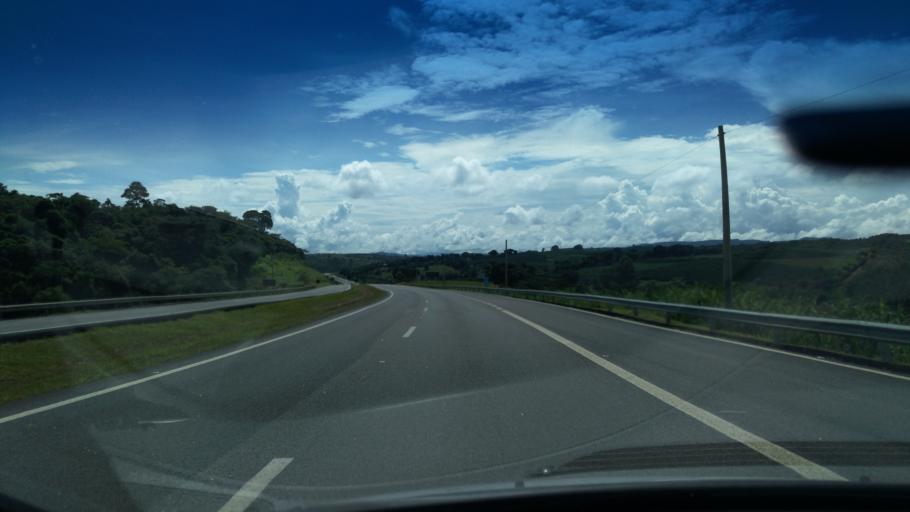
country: BR
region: Sao Paulo
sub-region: Santo Antonio Do Jardim
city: Espirito Santo do Pinhal
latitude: -22.2390
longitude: -46.8001
